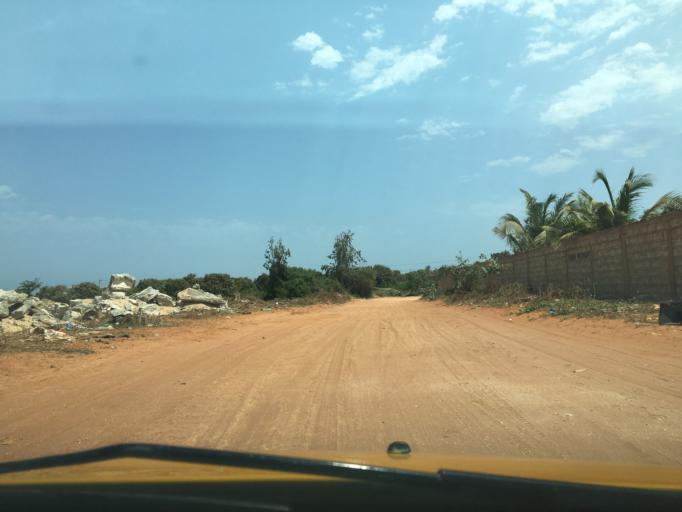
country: SN
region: Thies
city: Thies
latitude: 14.8077
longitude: -17.1901
